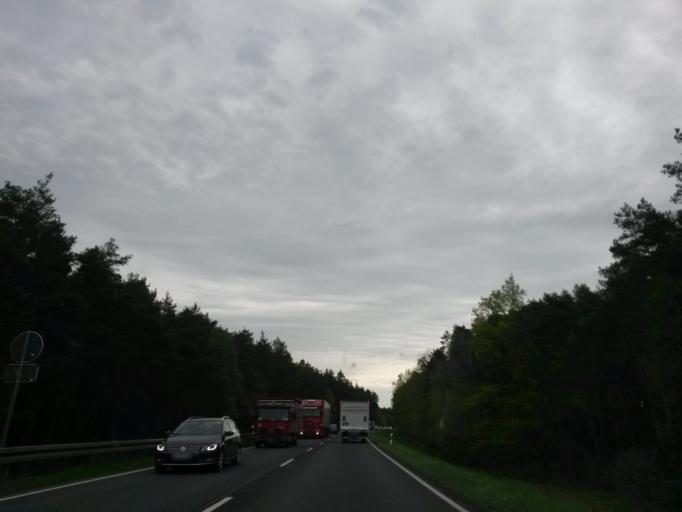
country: DE
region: Bavaria
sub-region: Upper Franconia
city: Frensdorf
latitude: 49.7714
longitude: 10.8842
